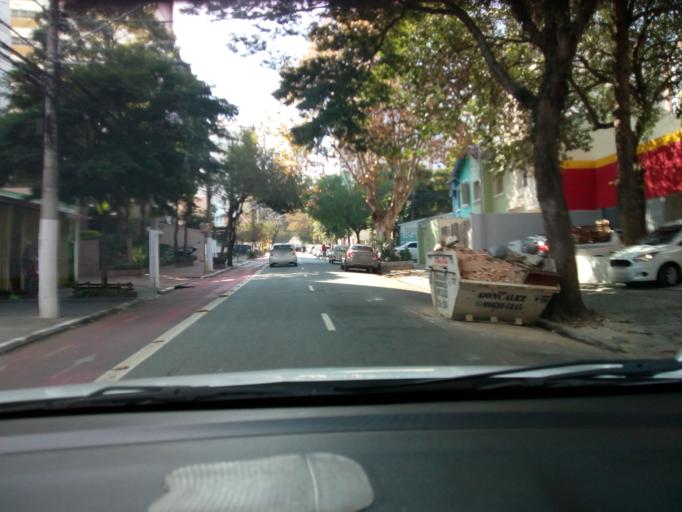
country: BR
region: Sao Paulo
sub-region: Sao Paulo
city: Sao Paulo
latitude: -23.5883
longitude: -46.6441
